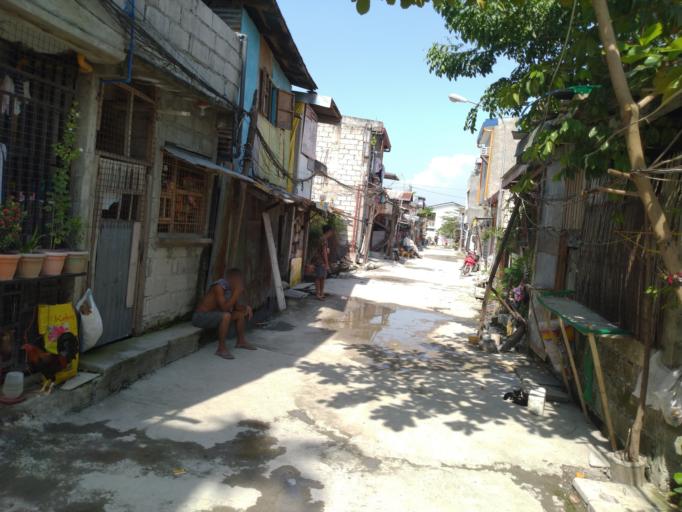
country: PH
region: Calabarzon
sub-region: Province of Rizal
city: Taytay
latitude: 14.5369
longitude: 121.1107
